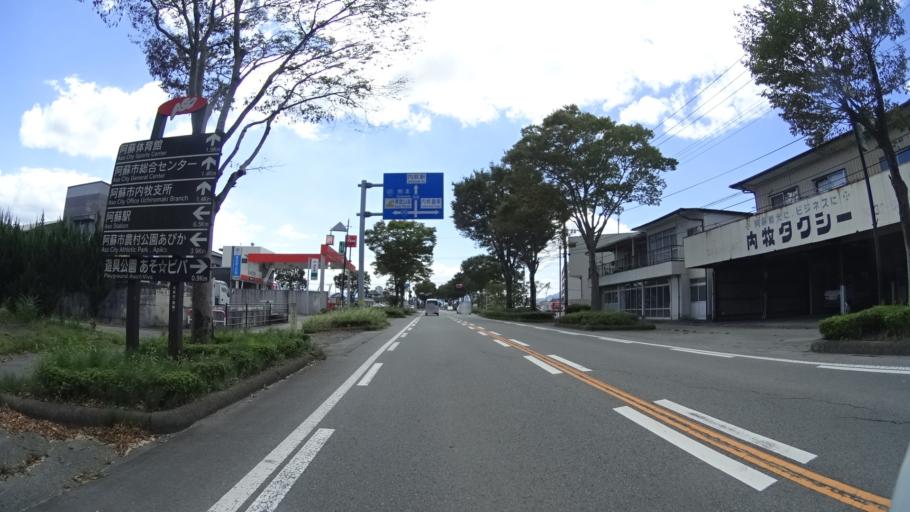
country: JP
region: Kumamoto
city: Aso
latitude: 32.9714
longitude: 131.0485
